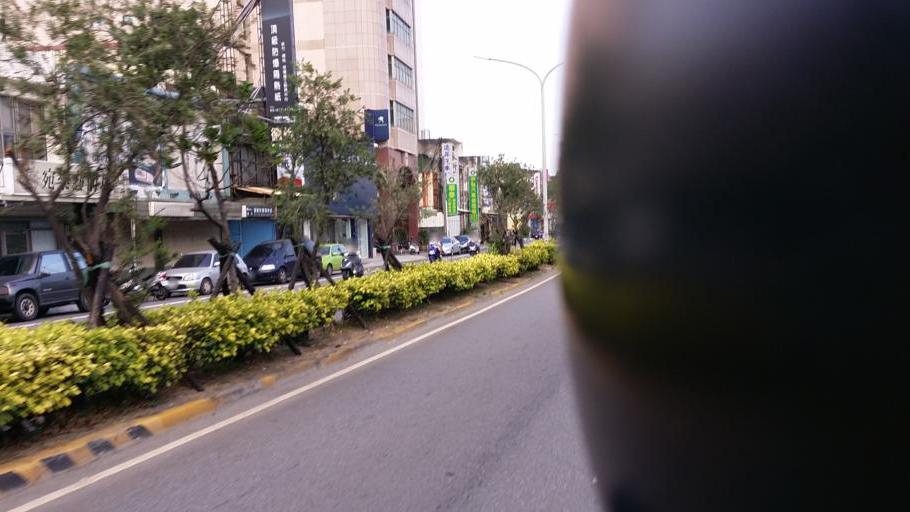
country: TW
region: Taiwan
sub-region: Hsinchu
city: Hsinchu
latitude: 24.8113
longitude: 120.9876
